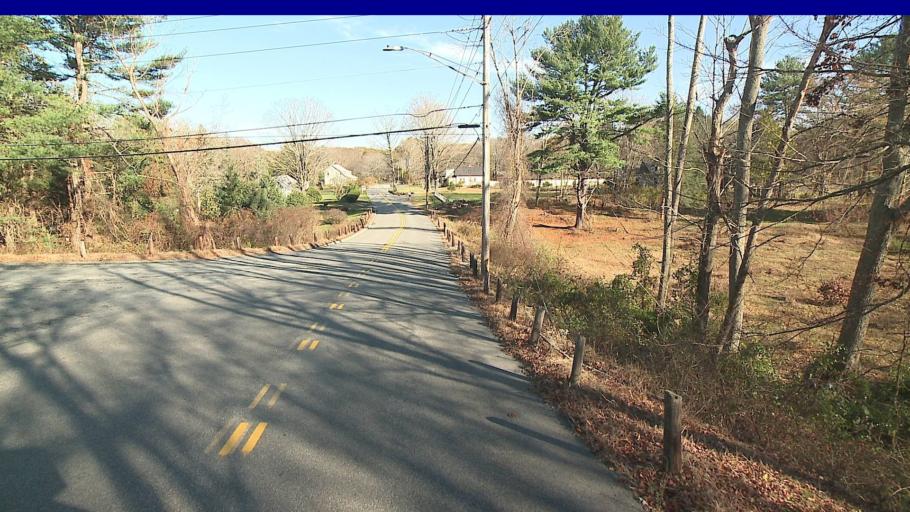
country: US
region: Connecticut
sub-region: Middlesex County
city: Lake Pocotopaug
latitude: 41.6068
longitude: -72.4939
